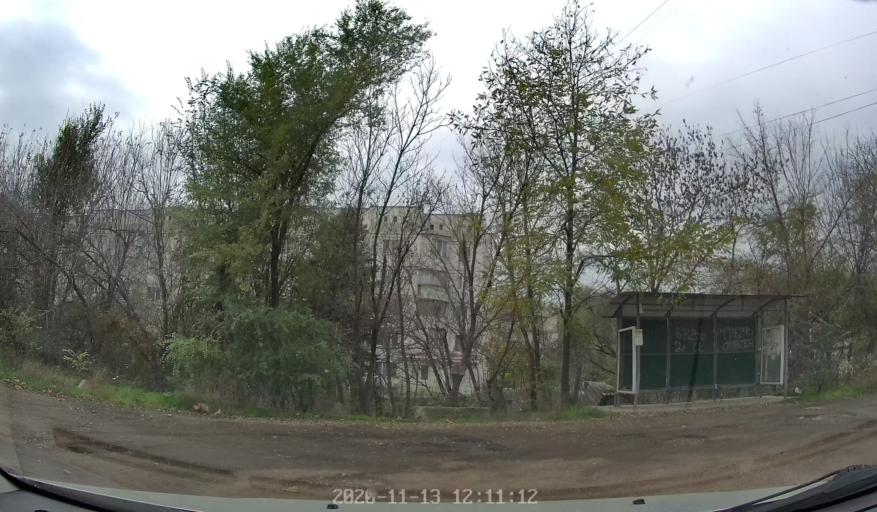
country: MD
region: Chisinau
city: Chisinau
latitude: 46.9567
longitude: 28.8376
